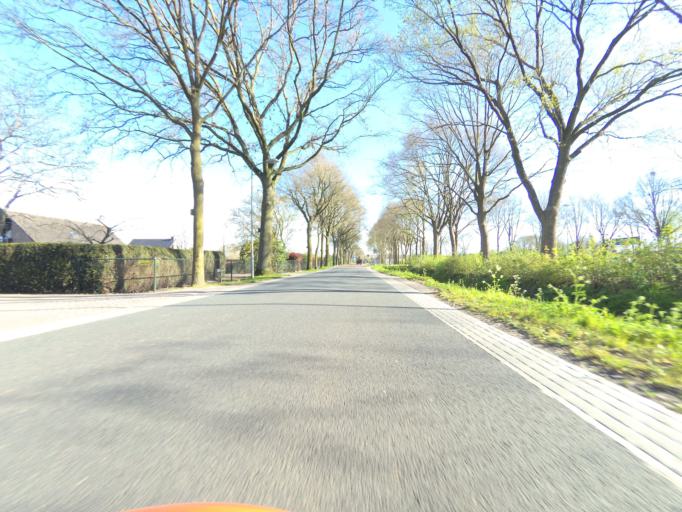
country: NL
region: Gelderland
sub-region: Gemeente Putten
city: Putten
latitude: 52.2514
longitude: 5.5920
